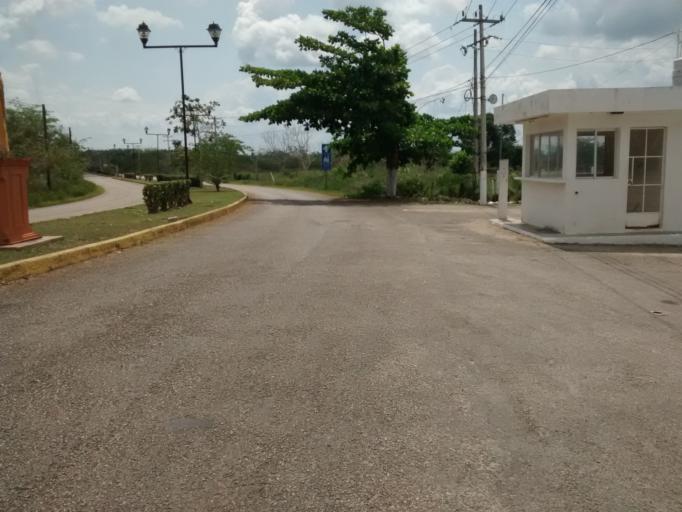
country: MX
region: Yucatan
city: Valladolid
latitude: 20.6874
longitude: -88.2238
